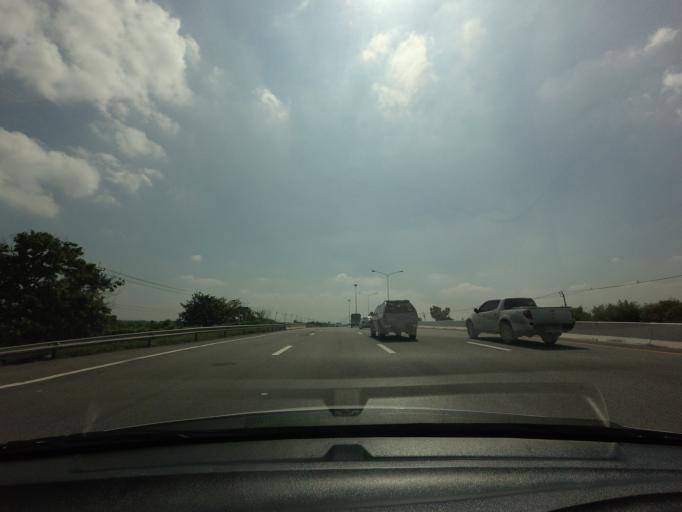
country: TH
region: Samut Prakan
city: Ban Khlong Bang Sao Thong
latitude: 13.6269
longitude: 100.9111
